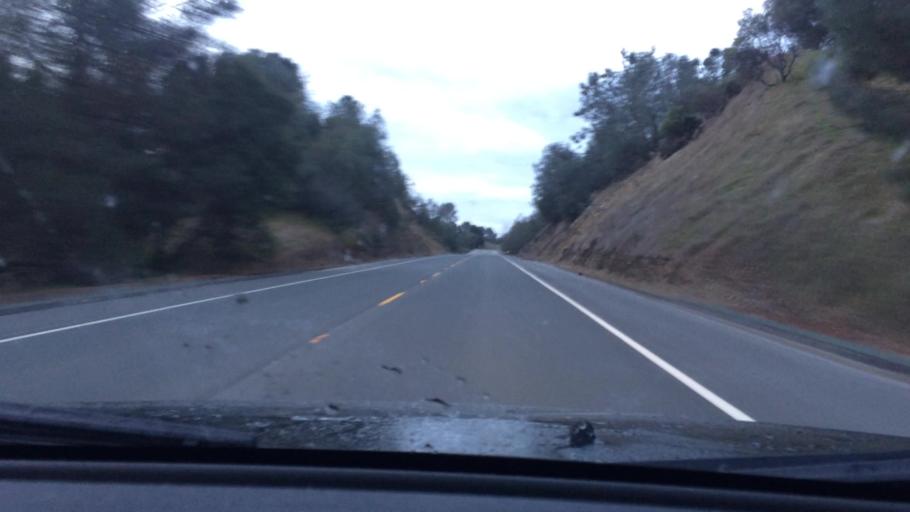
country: US
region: California
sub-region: Amador County
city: Ione
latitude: 38.4054
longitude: -120.8911
